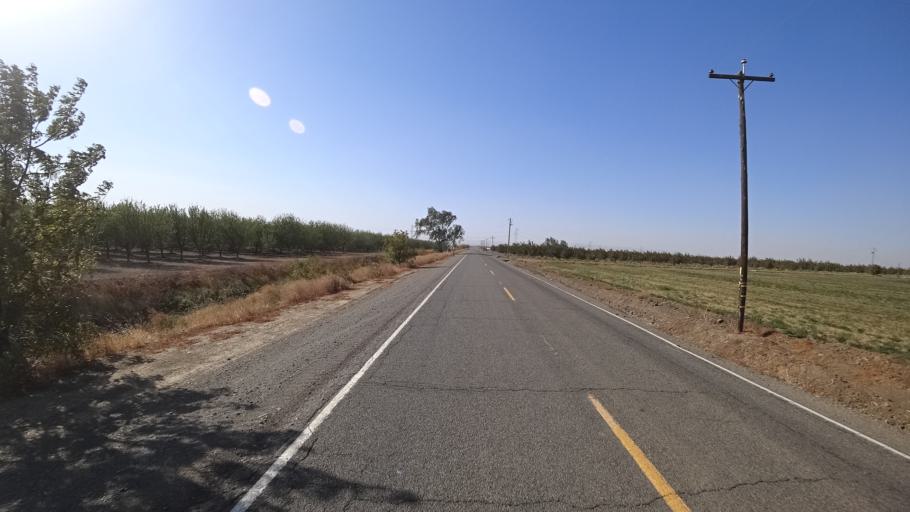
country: US
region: California
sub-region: Yolo County
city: Cottonwood
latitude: 38.7181
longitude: -121.9481
